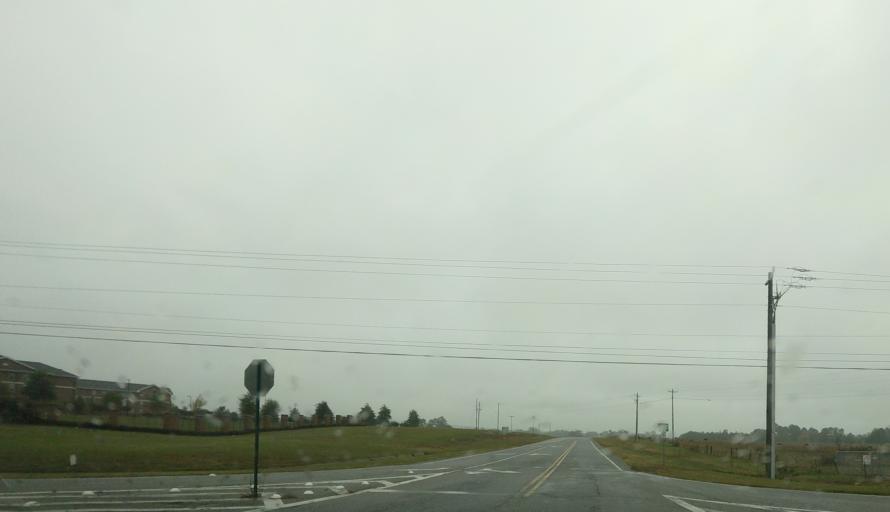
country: US
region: Georgia
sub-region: Peach County
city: Fort Valley
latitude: 32.5336
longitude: -83.9028
